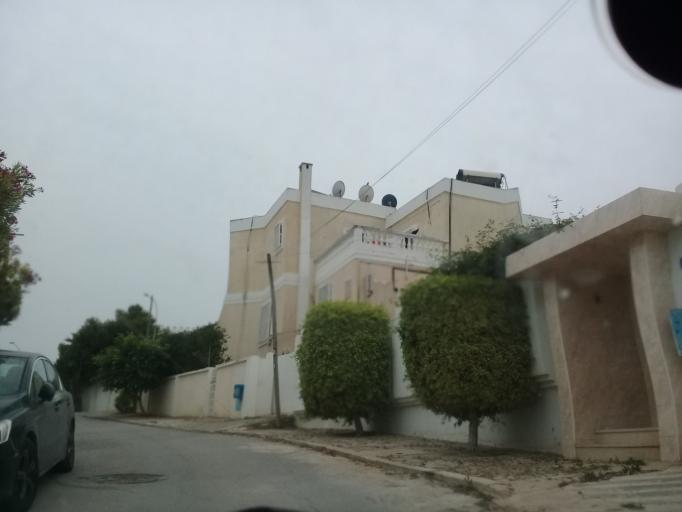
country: TN
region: Tunis
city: Tunis
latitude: 36.8460
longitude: 10.1485
